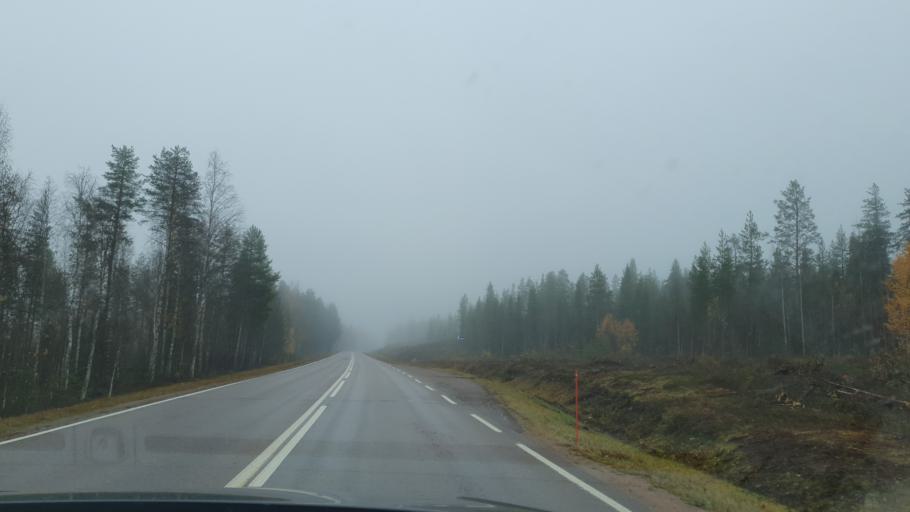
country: FI
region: Lapland
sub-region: Rovaniemi
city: Rovaniemi
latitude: 66.8137
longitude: 25.3997
